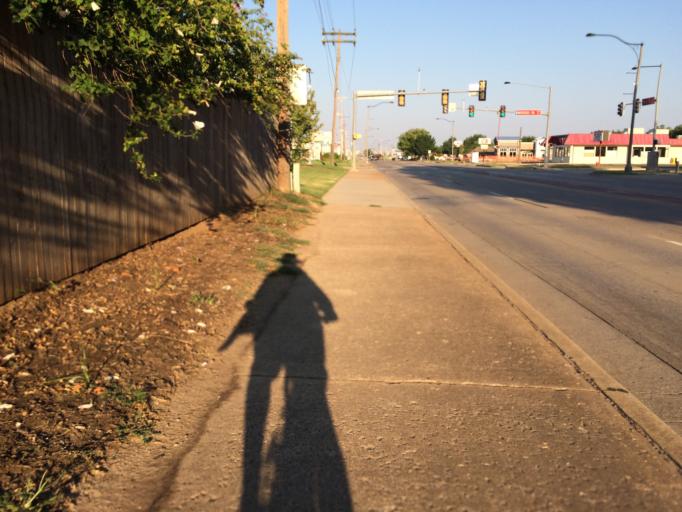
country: US
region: Oklahoma
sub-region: Cleveland County
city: Norman
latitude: 35.2184
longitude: -97.4676
